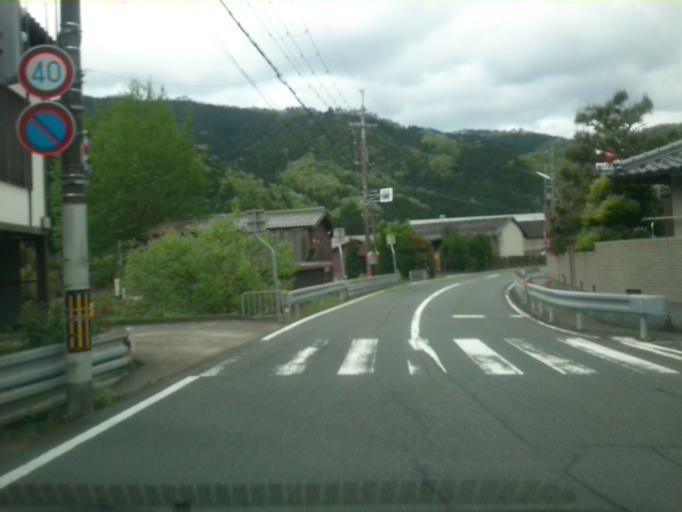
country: JP
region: Kyoto
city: Ayabe
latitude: 35.2593
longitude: 135.4013
